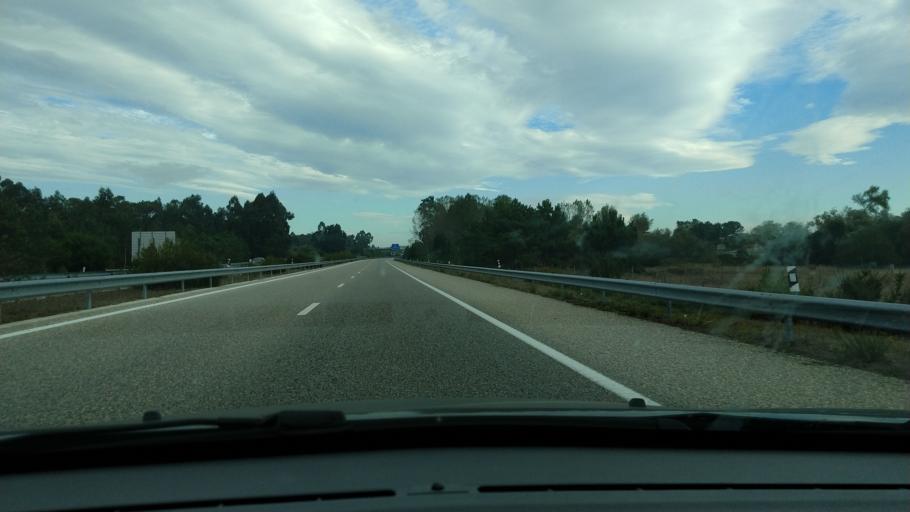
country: PT
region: Aveiro
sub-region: Vagos
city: Vagos
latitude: 40.4937
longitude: -8.6790
